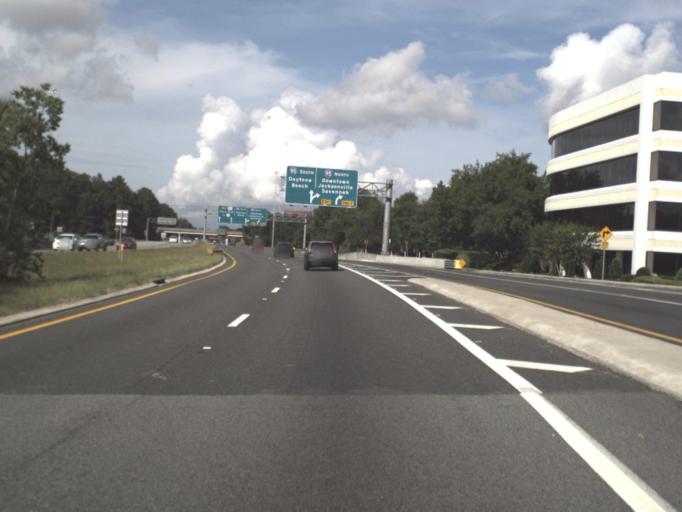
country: US
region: Florida
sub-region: Duval County
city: Jacksonville
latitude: 30.2513
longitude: -81.5891
